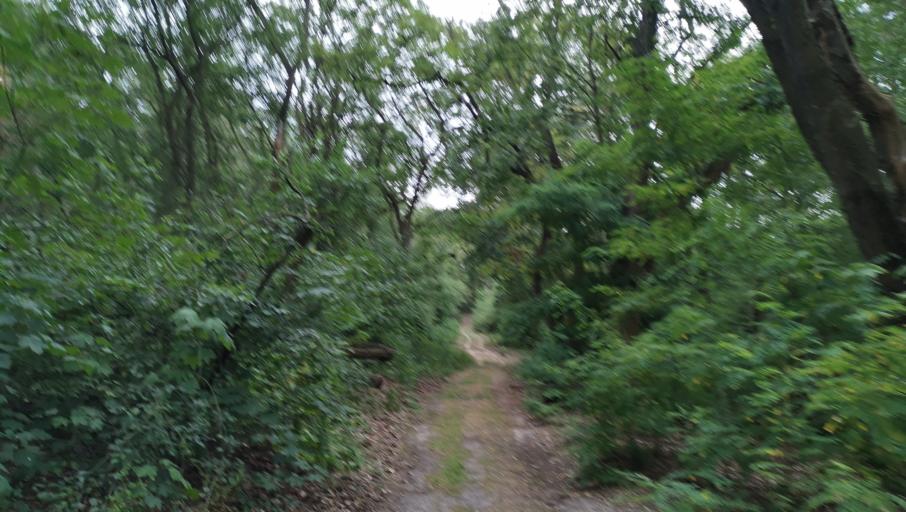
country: DE
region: Brandenburg
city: Potsdam
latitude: 52.3715
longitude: 13.0380
